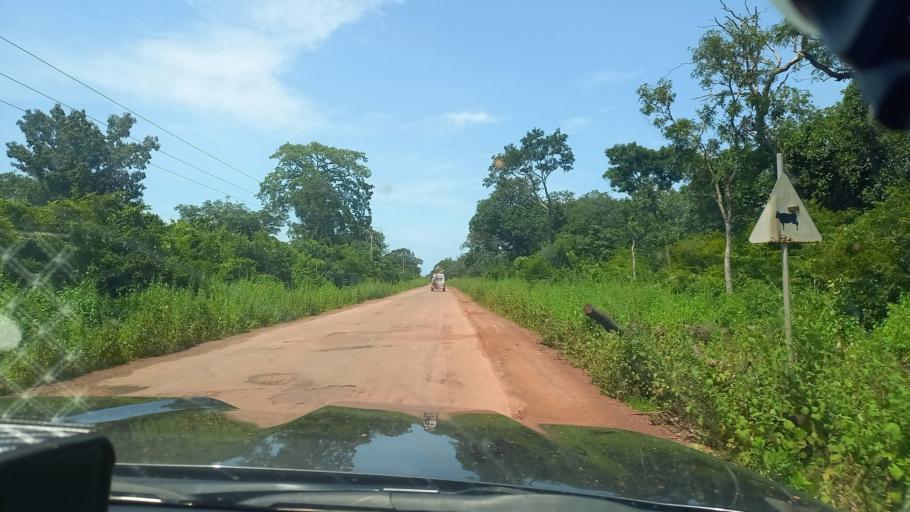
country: SN
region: Kolda
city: Marsassoum
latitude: 12.8576
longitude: -16.0983
